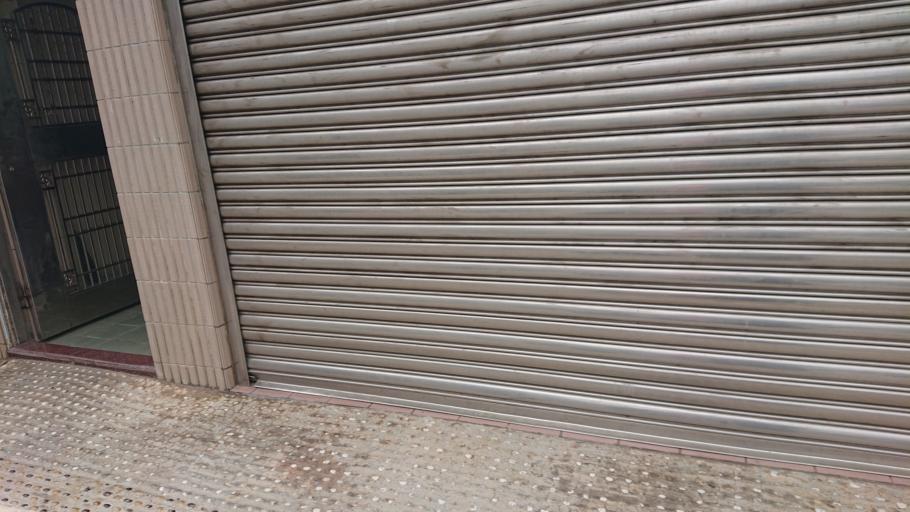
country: TW
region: Taiwan
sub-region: Penghu
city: Ma-kung
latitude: 23.5819
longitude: 119.5814
